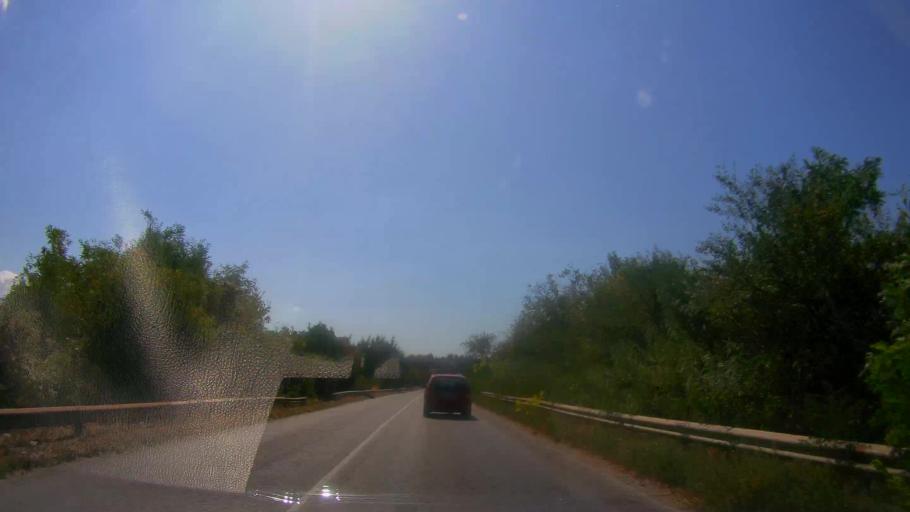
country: BG
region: Veliko Turnovo
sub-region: Obshtina Polski Trumbesh
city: Polski Trumbesh
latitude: 43.2700
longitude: 25.6436
